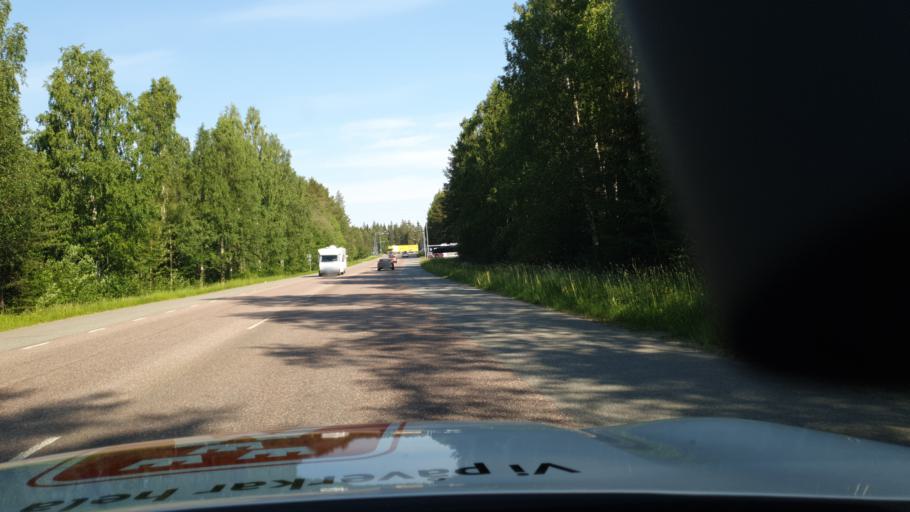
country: SE
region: Vaesterbotten
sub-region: Skelleftea Kommun
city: Skelleftea
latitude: 64.7590
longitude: 21.0077
